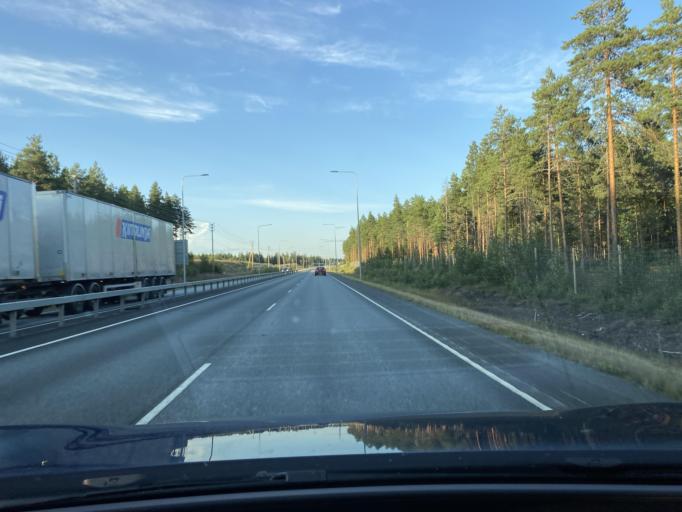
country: FI
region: Southern Ostrobothnia
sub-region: Seinaejoki
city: Seinaejoki
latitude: 62.7297
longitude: 22.8895
